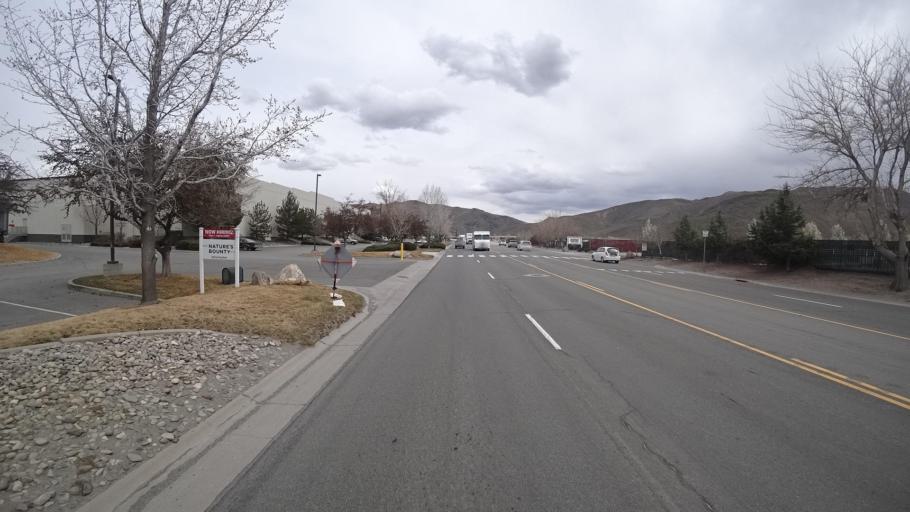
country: US
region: Nevada
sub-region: Washoe County
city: Sparks
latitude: 39.5214
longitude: -119.7168
